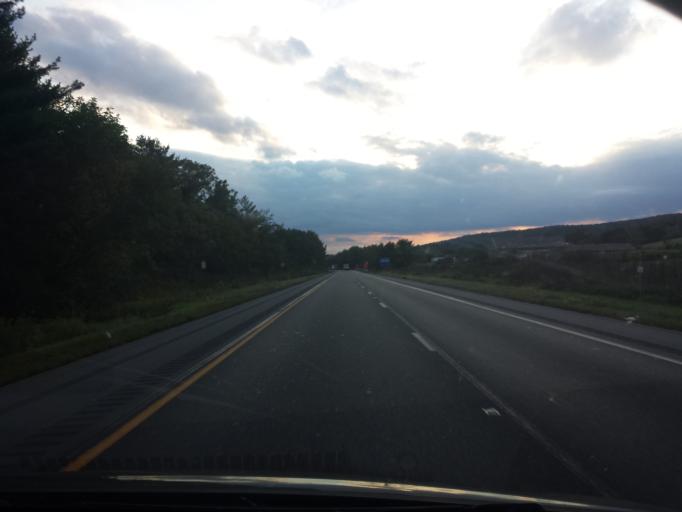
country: US
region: Pennsylvania
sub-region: Montour County
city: Danville
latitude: 40.9998
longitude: -76.6329
